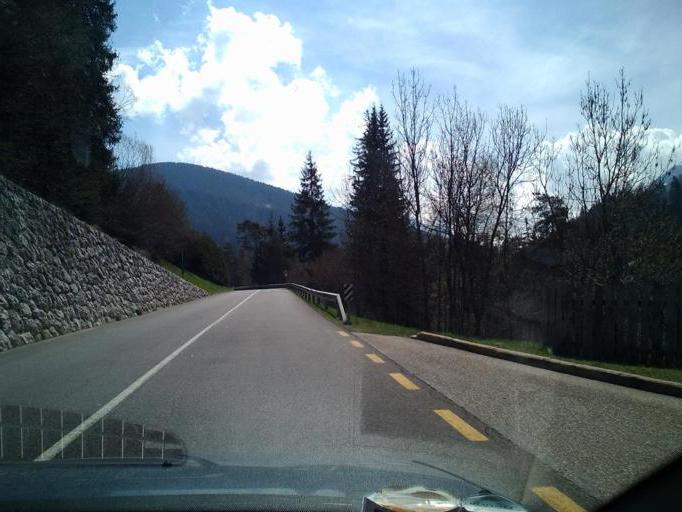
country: IT
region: Trentino-Alto Adige
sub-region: Bolzano
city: Braies
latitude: 46.7366
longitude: 12.1366
